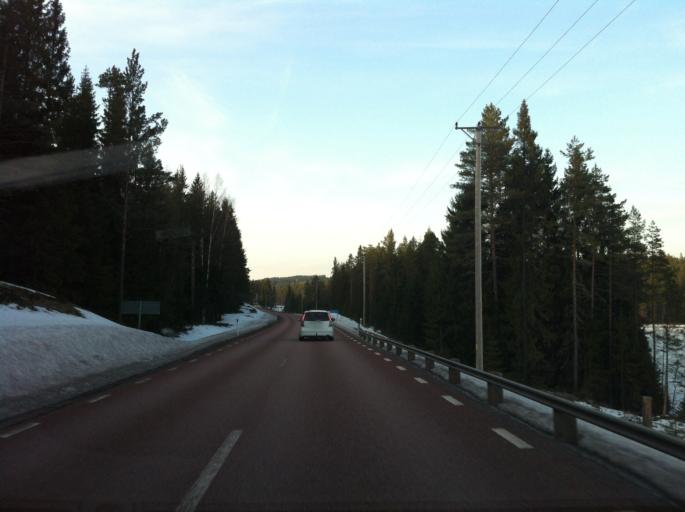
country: SE
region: Vaermland
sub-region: Filipstads Kommun
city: Lesjofors
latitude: 60.2440
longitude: 14.1807
